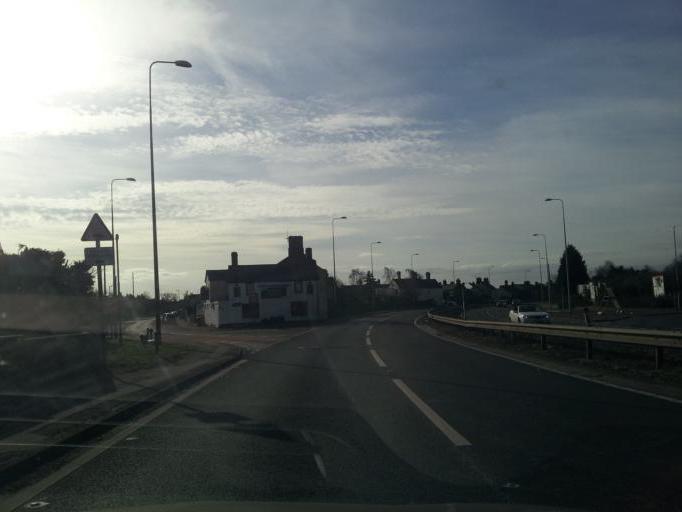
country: GB
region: England
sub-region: Central Bedfordshire
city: Sandy
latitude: 52.1382
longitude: -0.2985
